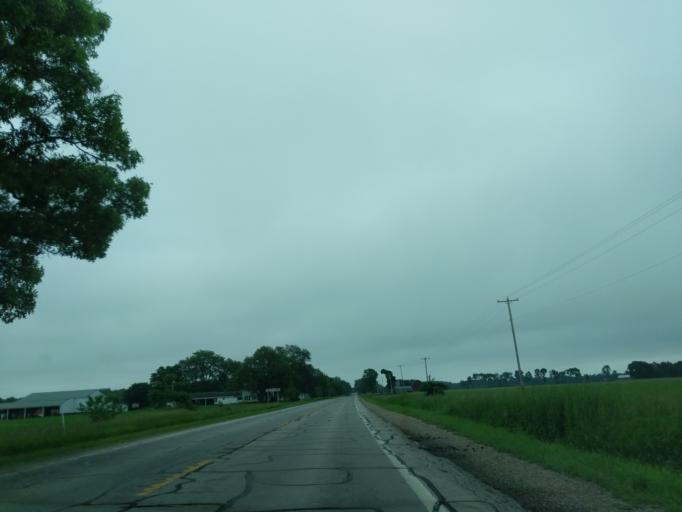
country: US
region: Michigan
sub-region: Hillsdale County
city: Litchfield
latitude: 42.0713
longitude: -84.7952
